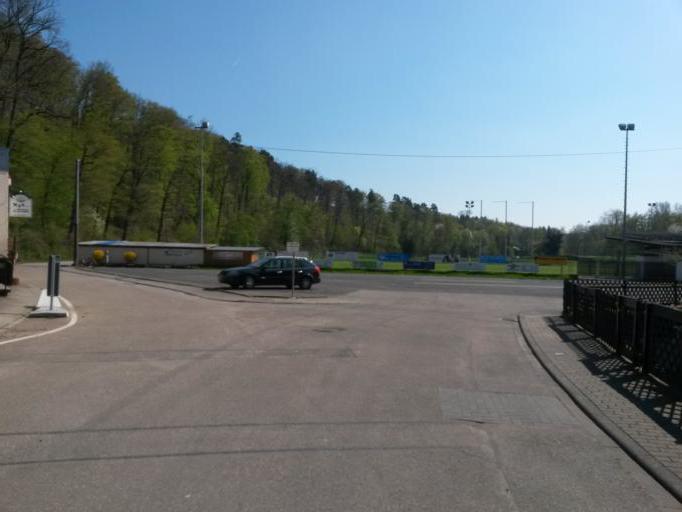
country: DE
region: Baden-Wuerttemberg
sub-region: Karlsruhe Region
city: Joehlingen
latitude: 48.9818
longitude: 8.5532
